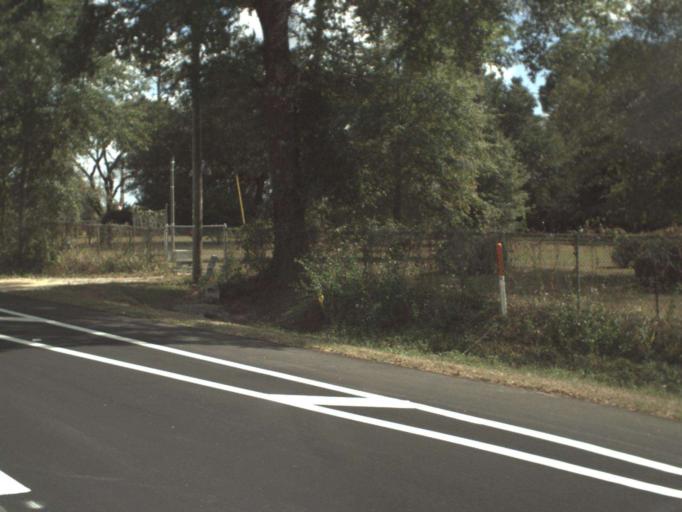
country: US
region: Florida
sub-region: Santa Rosa County
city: Pace
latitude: 30.6035
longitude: -87.1298
